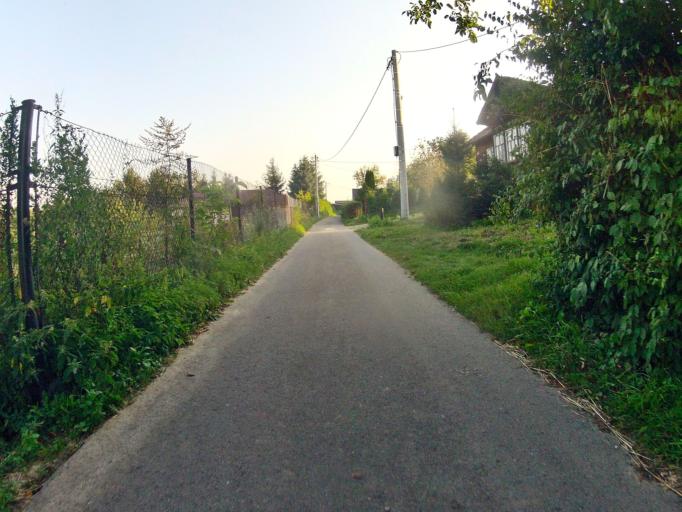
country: PL
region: Subcarpathian Voivodeship
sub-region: Powiat jasielski
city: Brzyska
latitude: 49.7858
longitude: 21.3917
